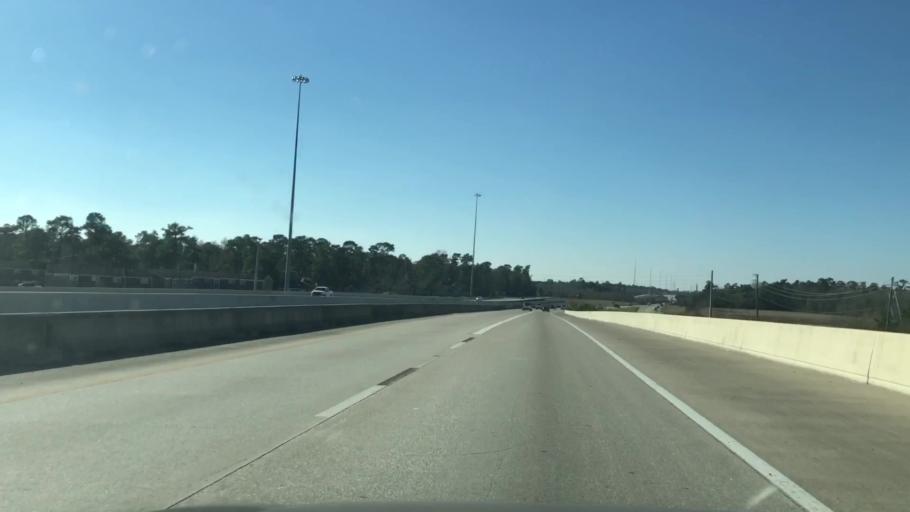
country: US
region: Texas
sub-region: Harris County
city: Cloverleaf
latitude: 29.8159
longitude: -95.2083
